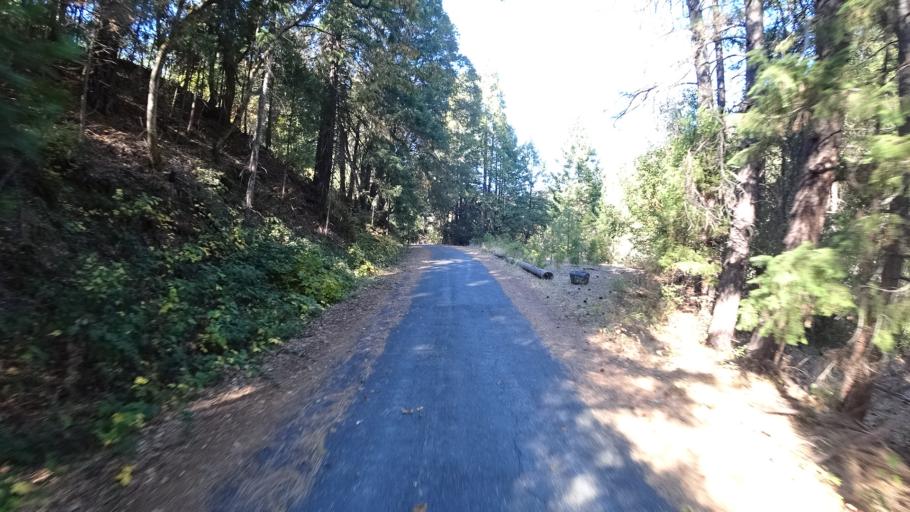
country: US
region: California
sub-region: Siskiyou County
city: Happy Camp
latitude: 41.7741
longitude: -123.0312
